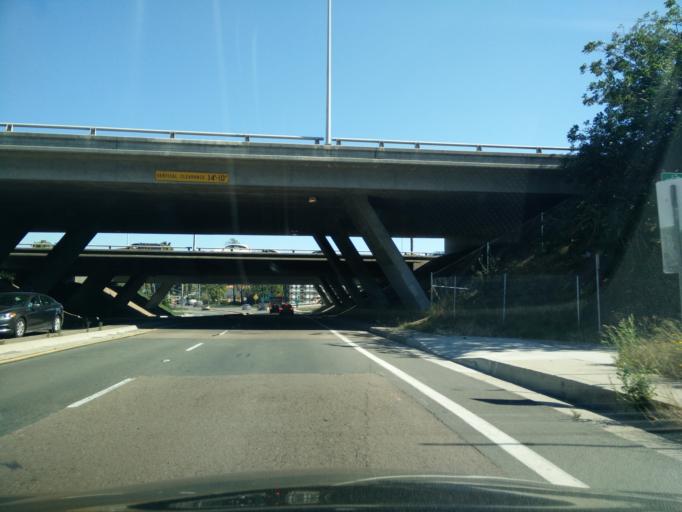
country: US
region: California
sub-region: San Diego County
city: San Diego
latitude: 32.7607
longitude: -117.1980
